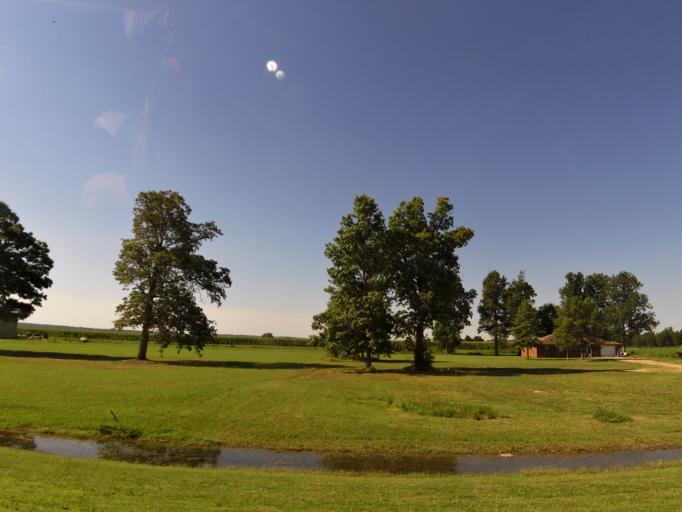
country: US
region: Arkansas
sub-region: Clay County
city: Rector
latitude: 36.4345
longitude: -90.3842
